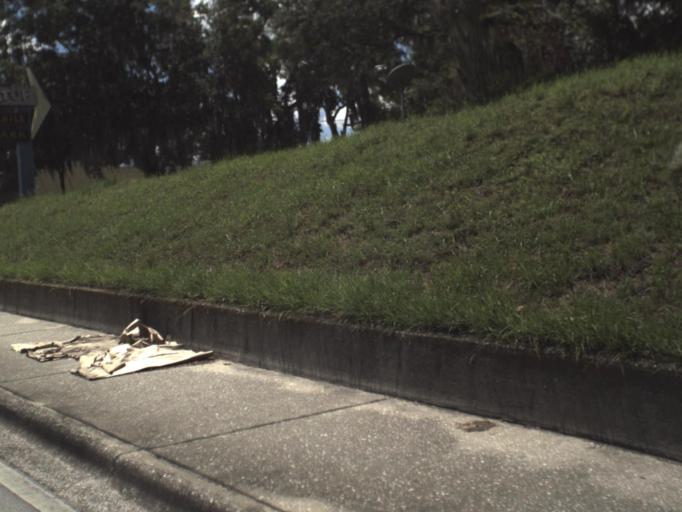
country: US
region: Florida
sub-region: Polk County
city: Lakeland
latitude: 28.0470
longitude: -81.9409
